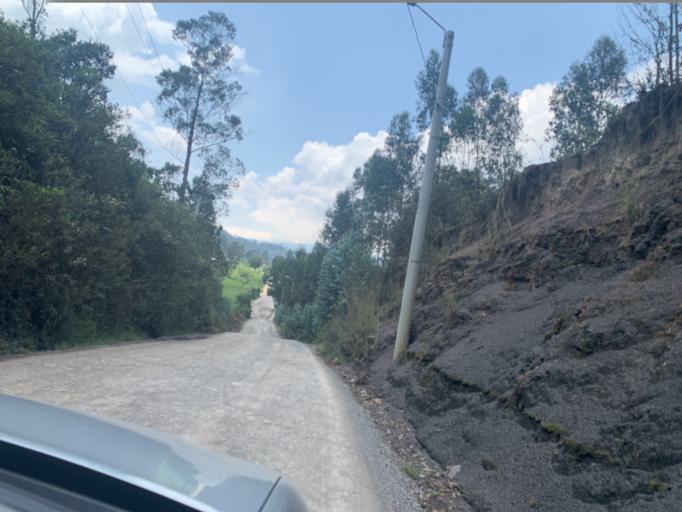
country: CO
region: Boyaca
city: Chiquinquira
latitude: 5.5983
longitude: -73.7623
